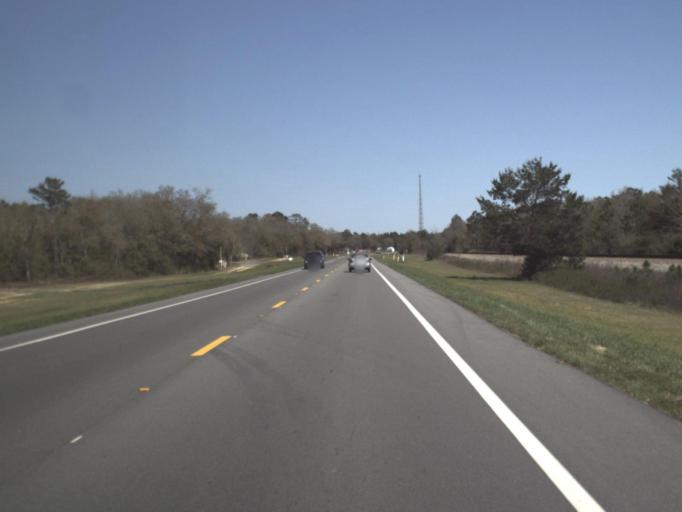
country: US
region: Florida
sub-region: Walton County
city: DeFuniak Springs
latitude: 30.7495
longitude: -86.2497
